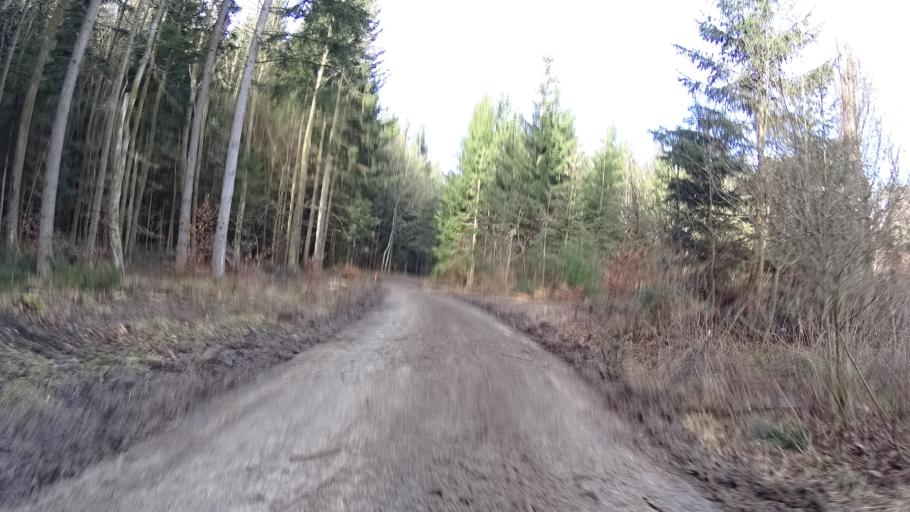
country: DE
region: Bavaria
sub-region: Upper Bavaria
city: Hitzhofen
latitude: 48.8813
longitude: 11.3147
